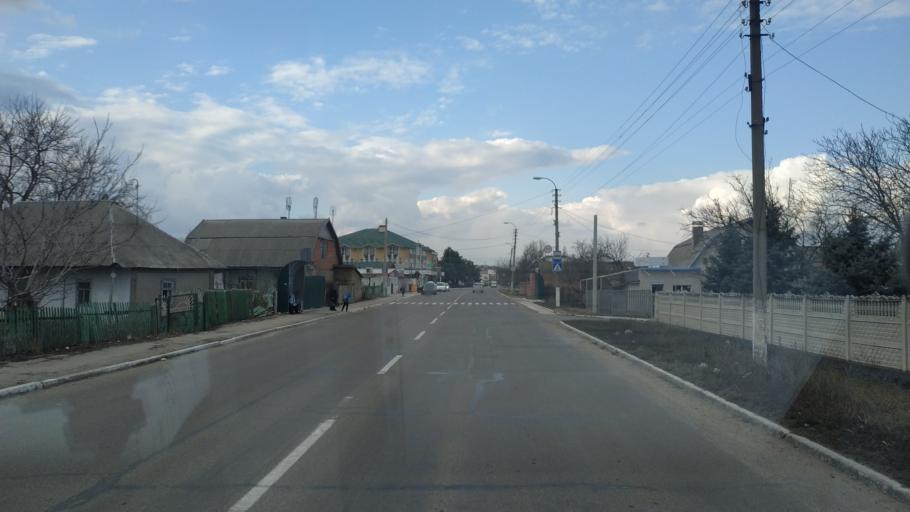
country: MD
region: Anenii Noi
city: Varnita
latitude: 46.8590
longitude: 29.4788
